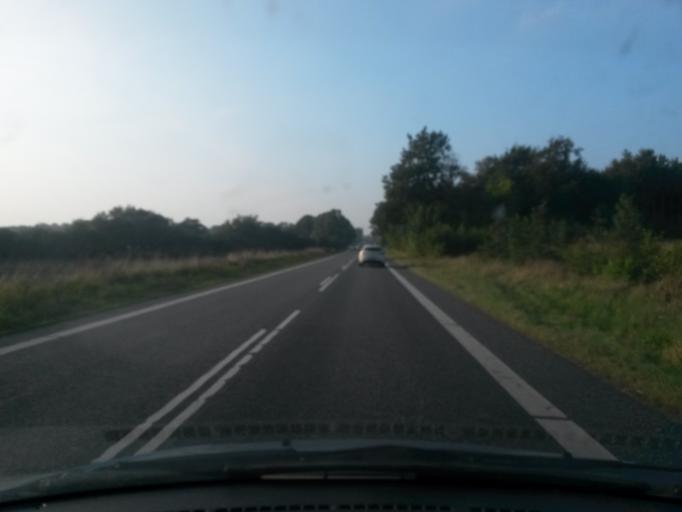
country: DK
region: Central Jutland
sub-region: Randers Kommune
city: Assentoft
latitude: 56.4071
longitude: 10.2352
